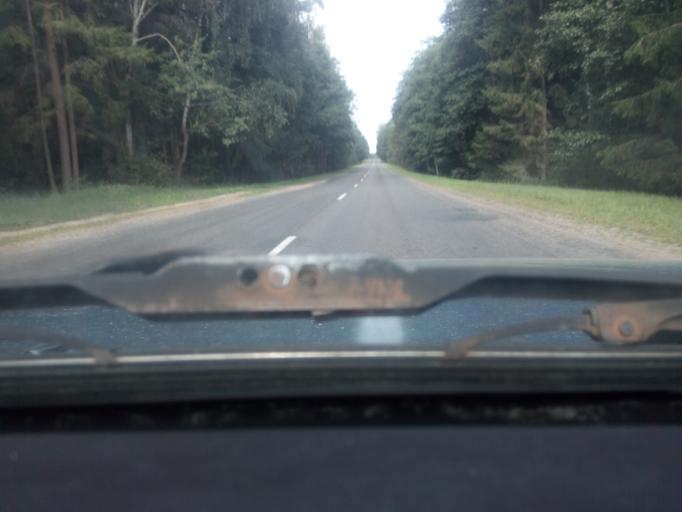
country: BY
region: Vitebsk
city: Vyerkhnyadzvinsk
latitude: 55.7948
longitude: 27.9634
